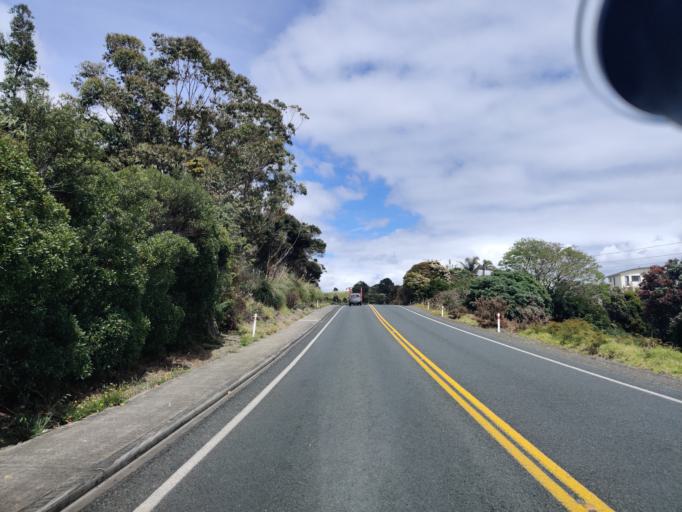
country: NZ
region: Northland
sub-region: Far North District
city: Taipa
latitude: -34.9928
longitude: 173.4956
